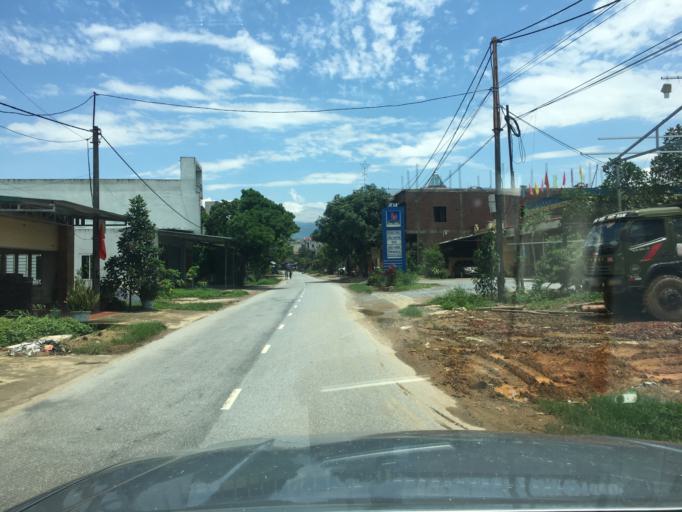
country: VN
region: Yen Bai
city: Son Thinh
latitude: 21.6423
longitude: 104.5006
